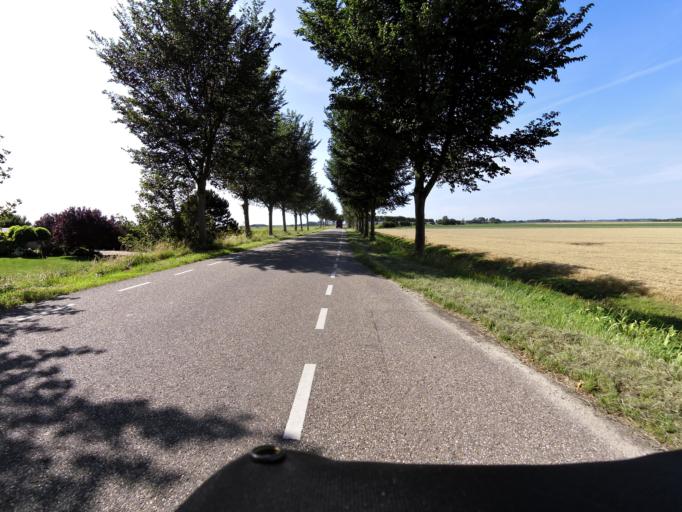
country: NL
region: South Holland
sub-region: Gemeente Goeree-Overflakkee
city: Dirksland
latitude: 51.7197
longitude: 4.0873
